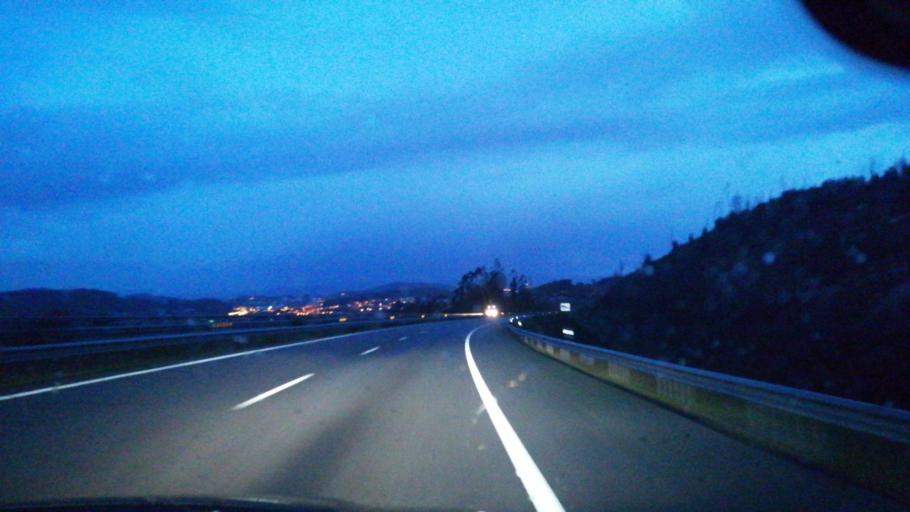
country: PT
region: Braga
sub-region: Vila Nova de Famalicao
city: Joane
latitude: 41.4838
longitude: -8.4052
